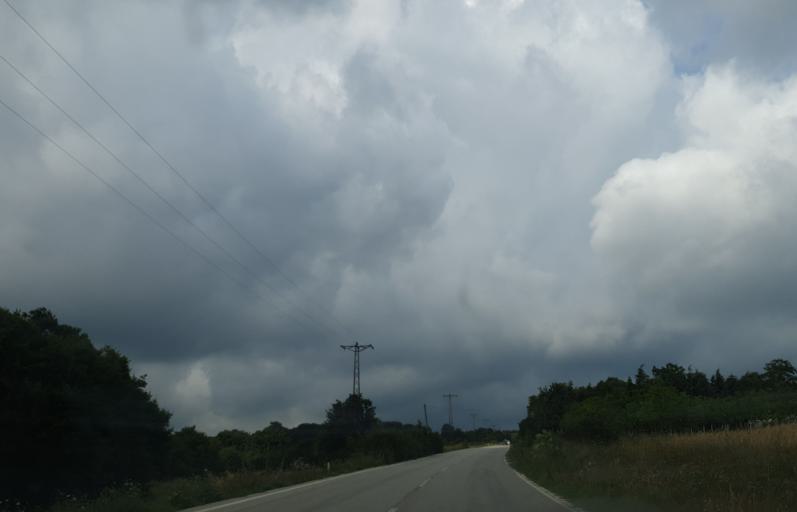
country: TR
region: Tekirdag
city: Saray
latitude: 41.4867
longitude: 27.9675
